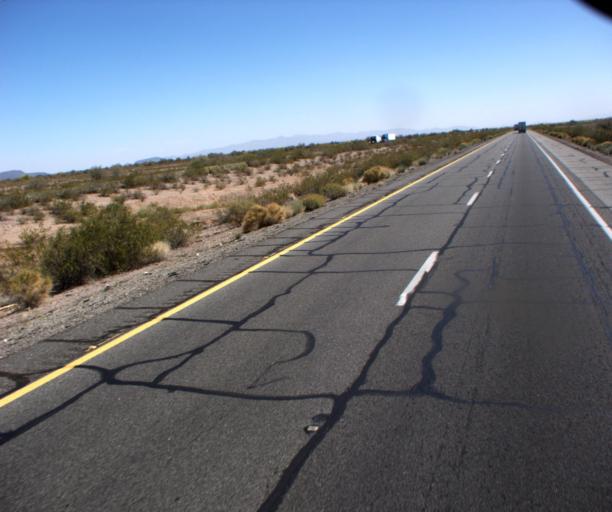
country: US
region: Arizona
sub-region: Maricopa County
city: Buckeye
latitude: 33.5104
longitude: -113.0111
